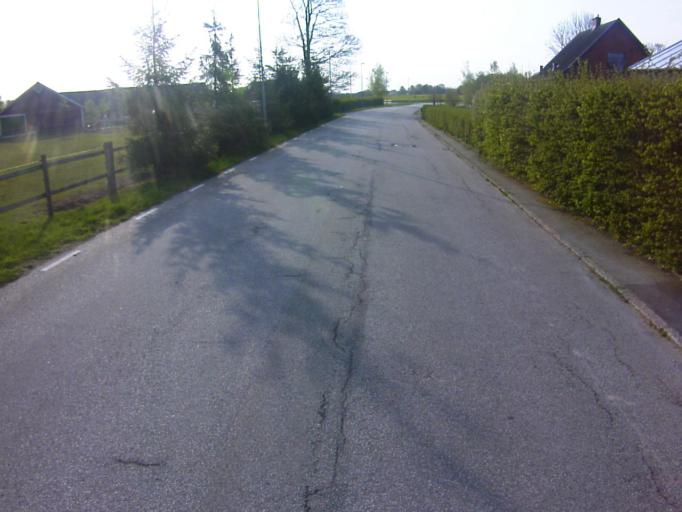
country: SE
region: Skane
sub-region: Kavlinge Kommun
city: Loddekopinge
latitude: 55.8212
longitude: 13.0343
